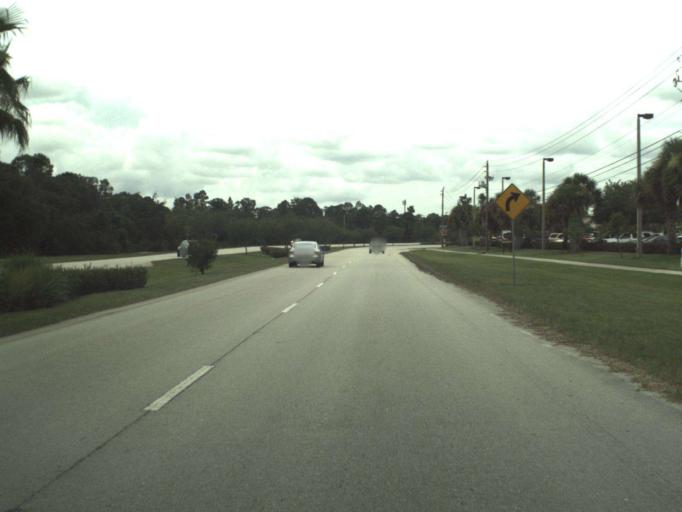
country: US
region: Florida
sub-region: Saint Lucie County
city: White City
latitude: 27.3565
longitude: -80.3576
